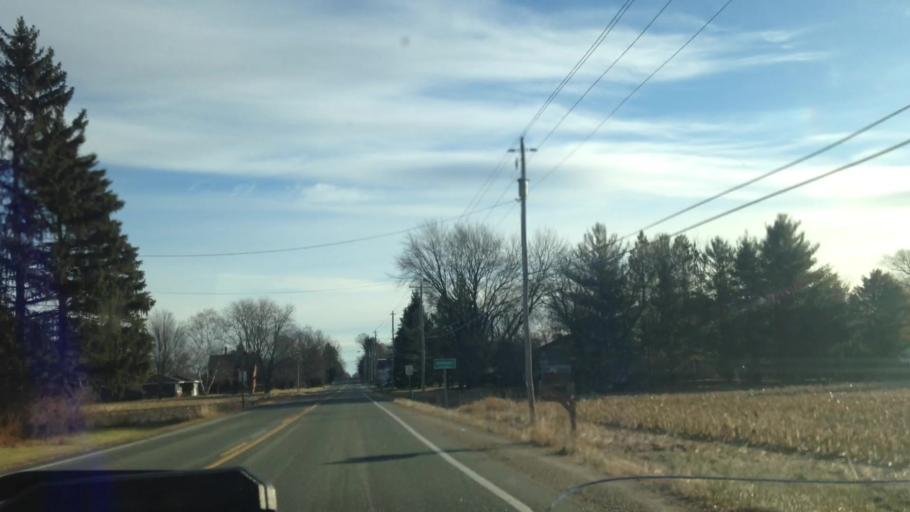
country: US
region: Wisconsin
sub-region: Washington County
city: Germantown
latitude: 43.2941
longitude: -88.1010
